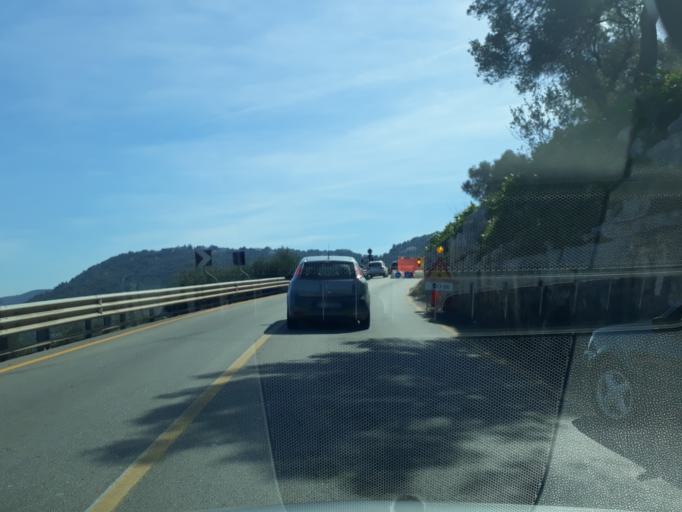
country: IT
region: Apulia
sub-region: Provincia di Brindisi
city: Lamie di Olimpie-Selva
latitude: 40.8143
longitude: 17.3461
